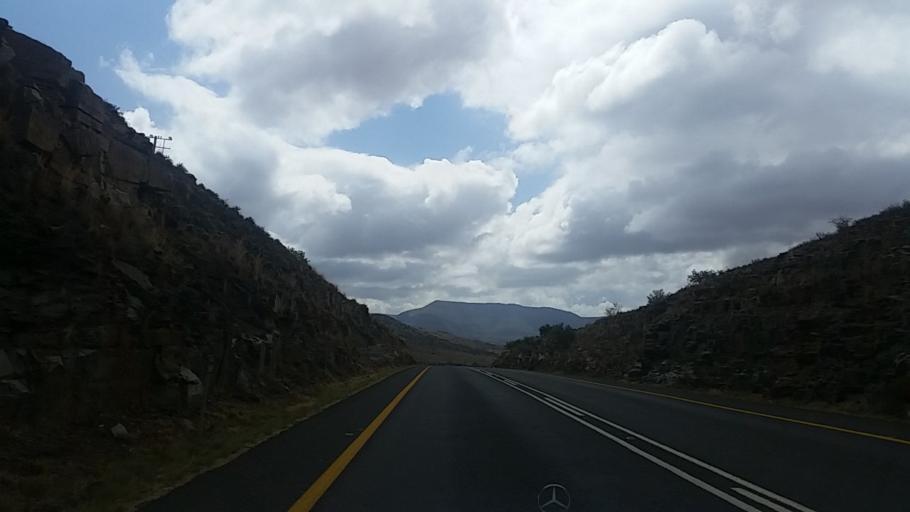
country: ZA
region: Eastern Cape
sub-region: Cacadu District Municipality
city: Graaff-Reinet
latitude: -32.1086
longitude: 24.6082
